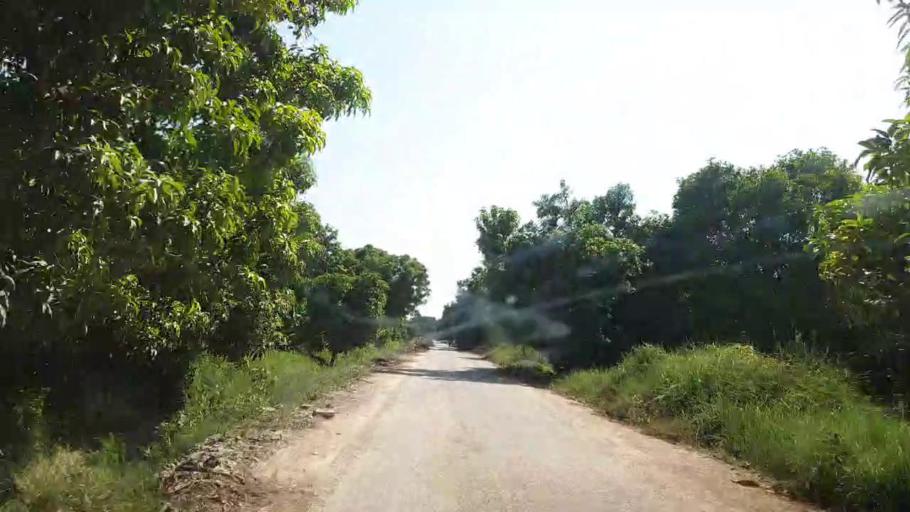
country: PK
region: Sindh
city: Tando Jam
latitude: 25.4089
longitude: 68.5821
